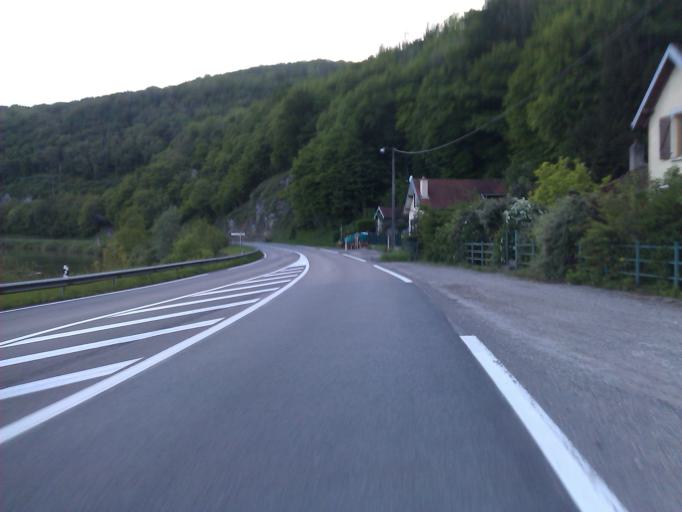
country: FR
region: Franche-Comte
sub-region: Departement du Doubs
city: Baume-les-Dames
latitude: 47.3726
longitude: 6.4266
